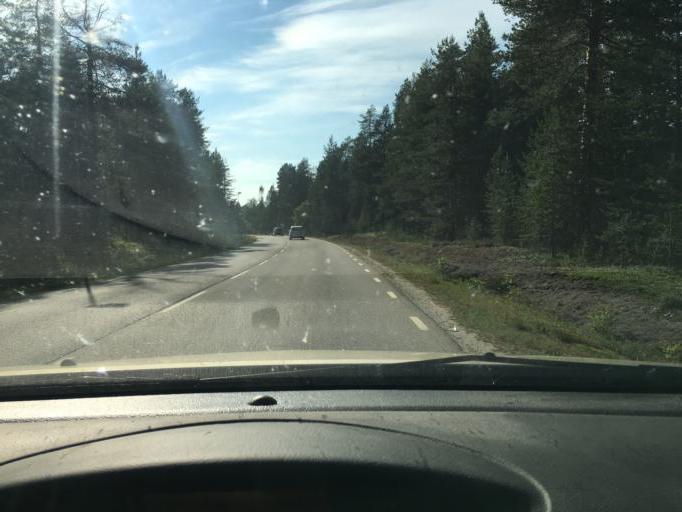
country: SE
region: Norrbotten
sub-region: Lulea Kommun
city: Bergnaset
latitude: 65.5953
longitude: 22.0568
